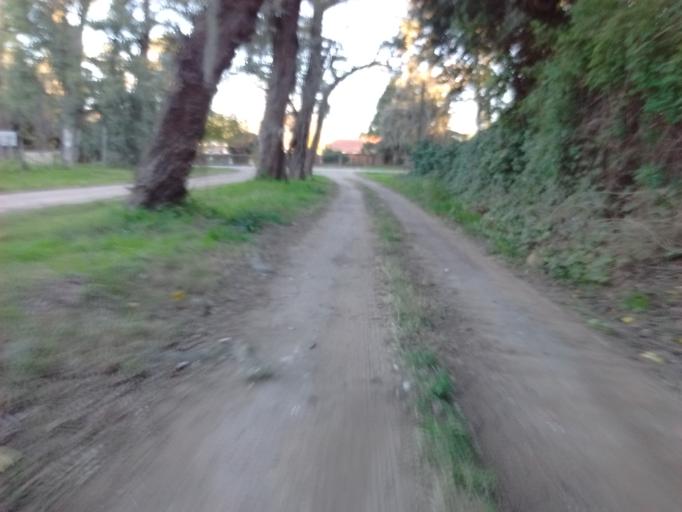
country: AR
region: Santa Fe
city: Funes
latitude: -32.9173
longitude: -60.8328
